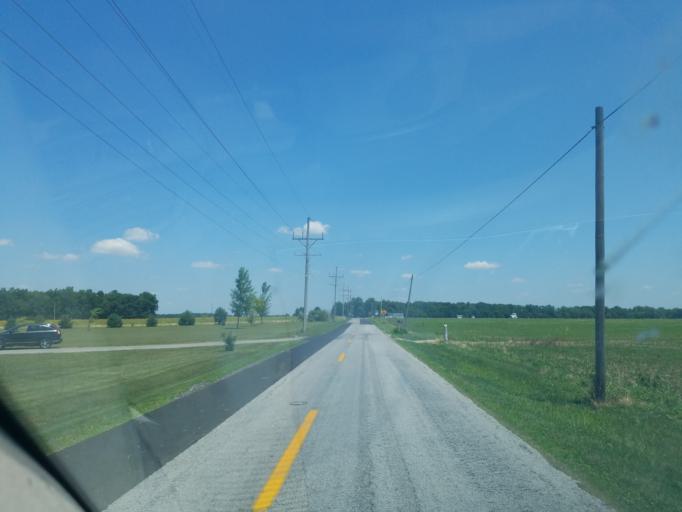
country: US
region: Ohio
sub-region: Allen County
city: Delphos
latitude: 40.7847
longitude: -84.3039
